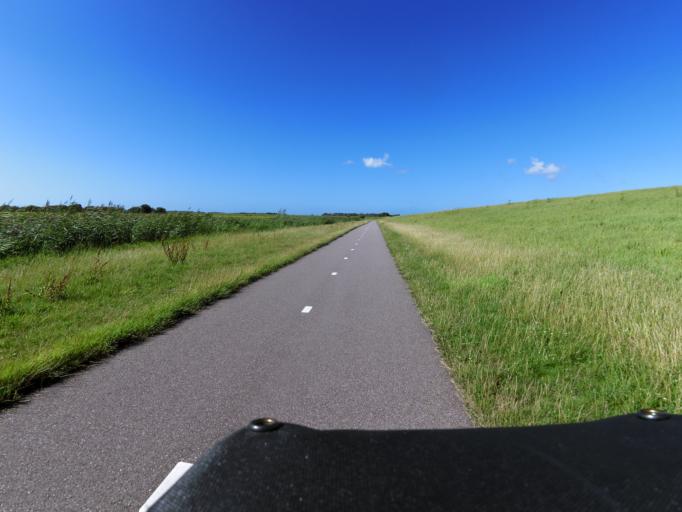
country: NL
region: South Holland
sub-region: Gemeente Goeree-Overflakkee
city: Dirksland
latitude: 51.7798
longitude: 4.0384
